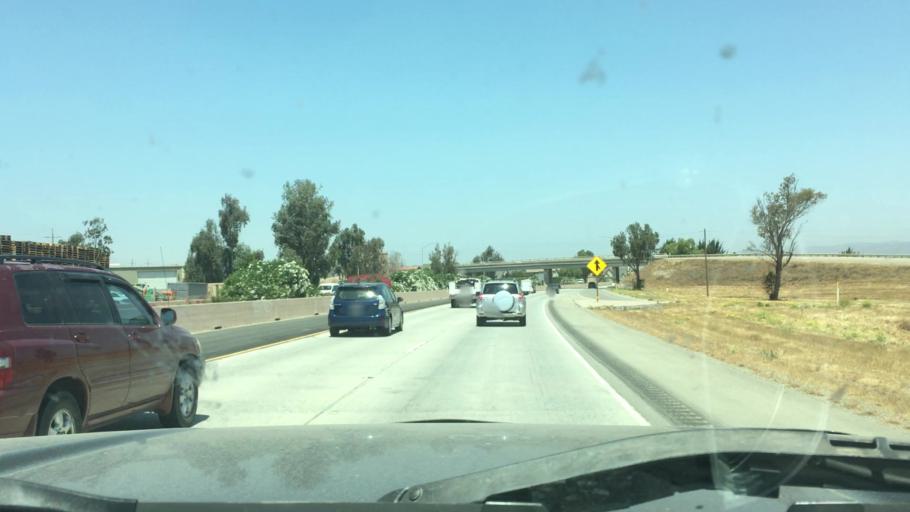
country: US
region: California
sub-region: Monterey County
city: Greenfield
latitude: 36.3123
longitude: -121.2330
